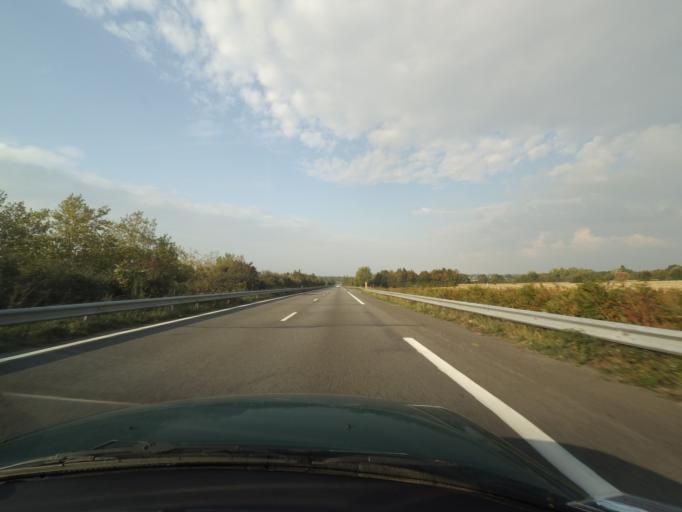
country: FR
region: Pays de la Loire
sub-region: Departement de la Loire-Atlantique
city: Jans
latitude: 47.5983
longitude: -1.6275
